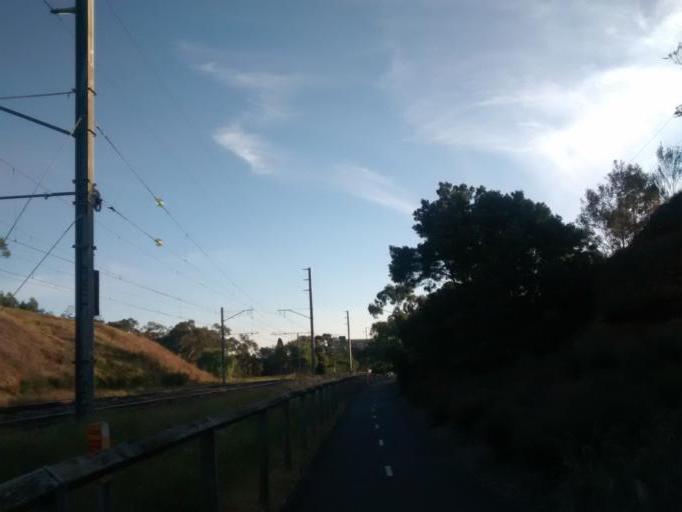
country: AU
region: Victoria
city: Parkville
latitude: -37.7854
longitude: 144.9442
